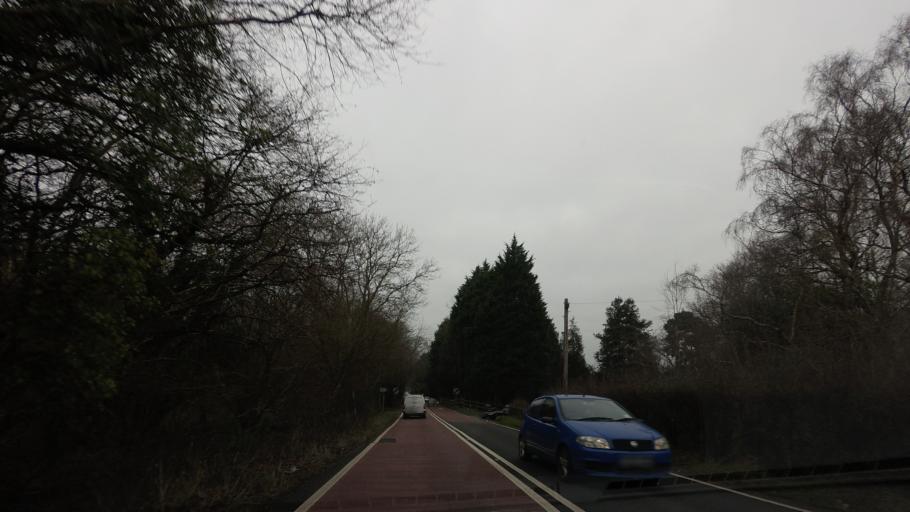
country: GB
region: England
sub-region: East Sussex
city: Saint Leonards-on-Sea
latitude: 50.9011
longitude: 0.5534
